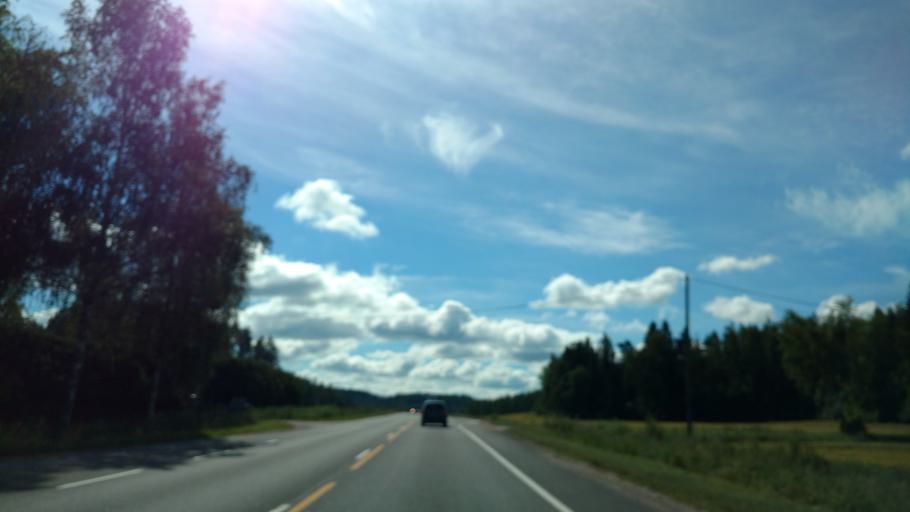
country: FI
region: Varsinais-Suomi
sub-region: Salo
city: Salo
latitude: 60.3676
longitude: 23.1371
